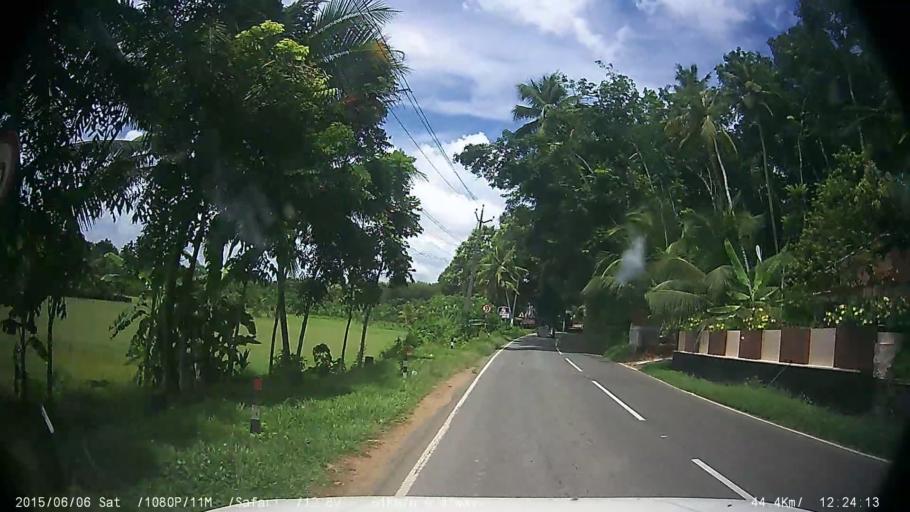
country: IN
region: Kerala
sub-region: Kottayam
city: Palackattumala
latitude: 9.6597
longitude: 76.6120
